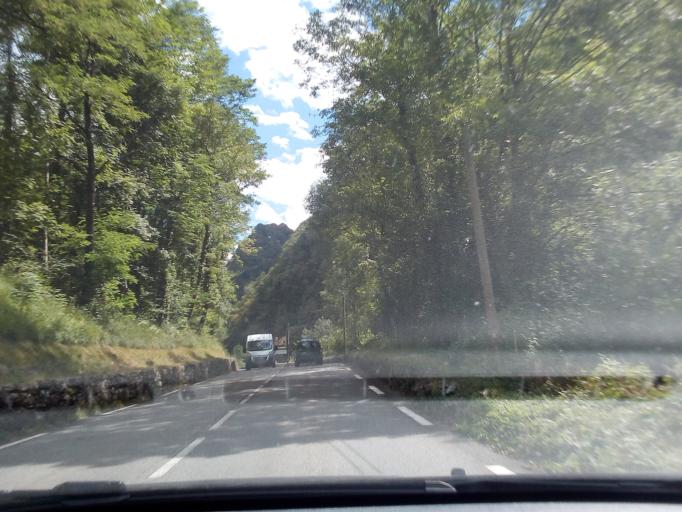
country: FR
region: Aquitaine
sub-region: Departement des Pyrenees-Atlantiques
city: Laruns
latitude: 42.9256
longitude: -0.5799
